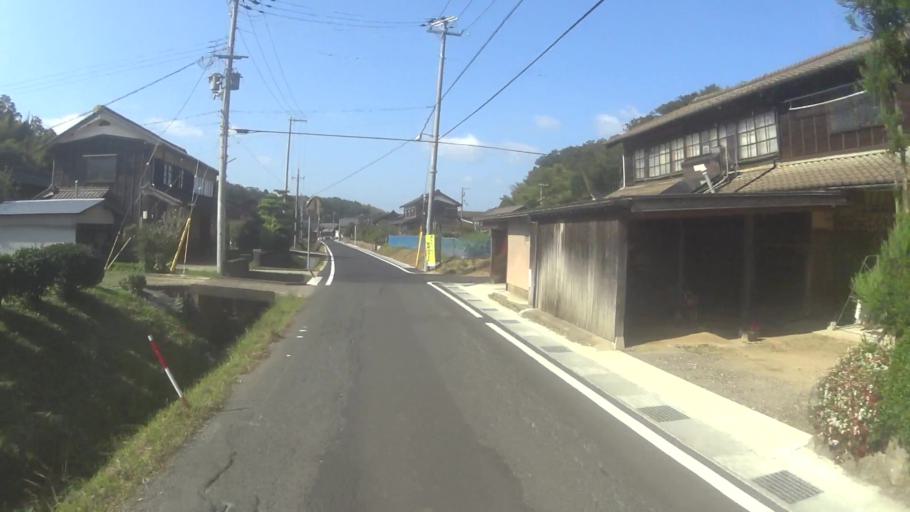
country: JP
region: Kyoto
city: Miyazu
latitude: 35.6763
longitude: 135.0543
